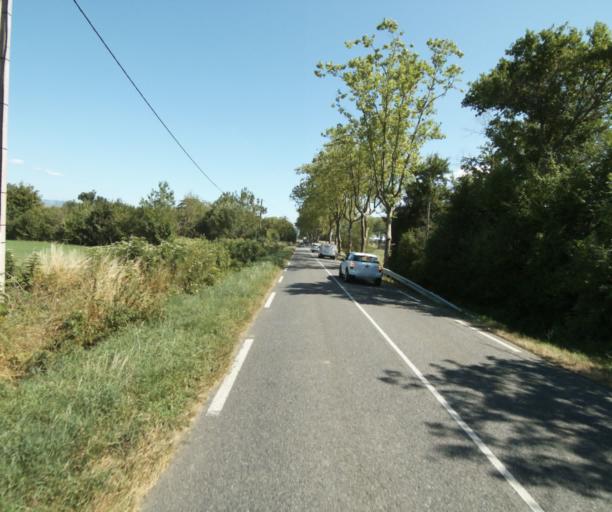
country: FR
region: Midi-Pyrenees
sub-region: Departement de la Haute-Garonne
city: Saint-Felix-Lauragais
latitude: 43.4914
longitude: 1.9027
